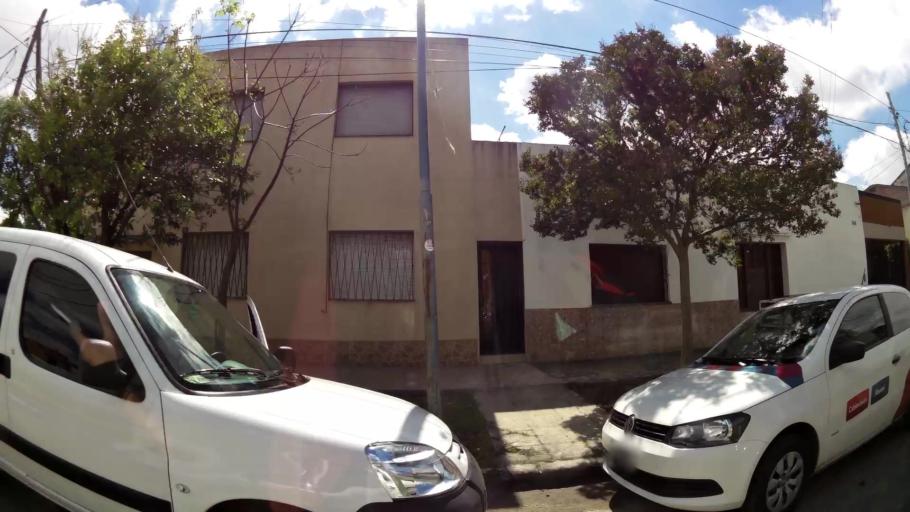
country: AR
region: Buenos Aires
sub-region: Partido de Lanus
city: Lanus
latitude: -34.6872
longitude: -58.4242
